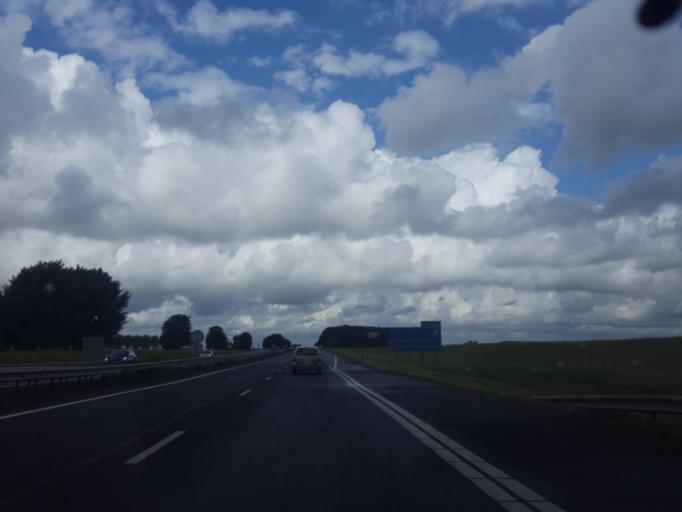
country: NL
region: North Brabant
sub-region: Gemeente Moerdijk
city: Willemstad
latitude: 51.7429
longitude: 4.4127
